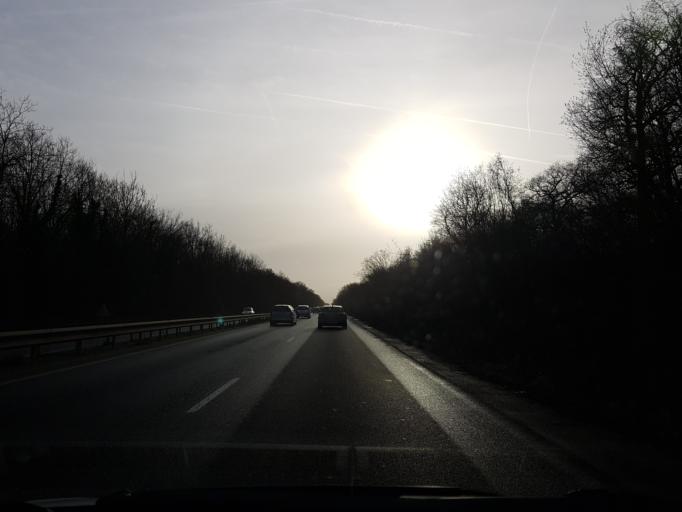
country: FR
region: Ile-de-France
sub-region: Departement de l'Essonne
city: Epinay-sous-Senart
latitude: 48.6744
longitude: 2.5008
